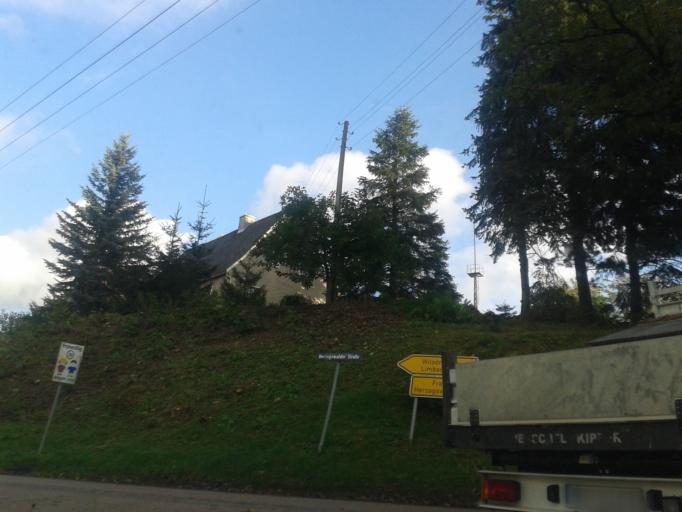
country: DE
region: Saxony
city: Wilsdruff
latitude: 51.0283
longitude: 13.4705
